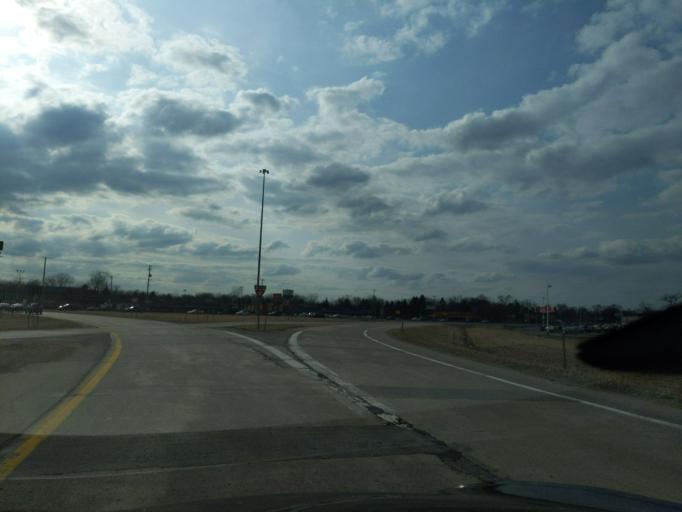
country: US
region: Michigan
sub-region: Ingham County
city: Holt
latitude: 42.6662
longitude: -84.5400
